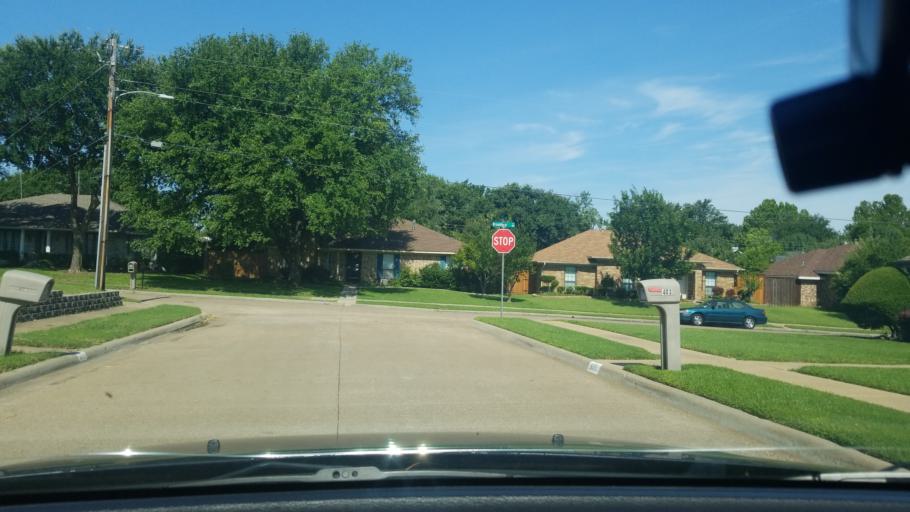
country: US
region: Texas
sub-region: Dallas County
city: Mesquite
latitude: 32.7760
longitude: -96.5920
